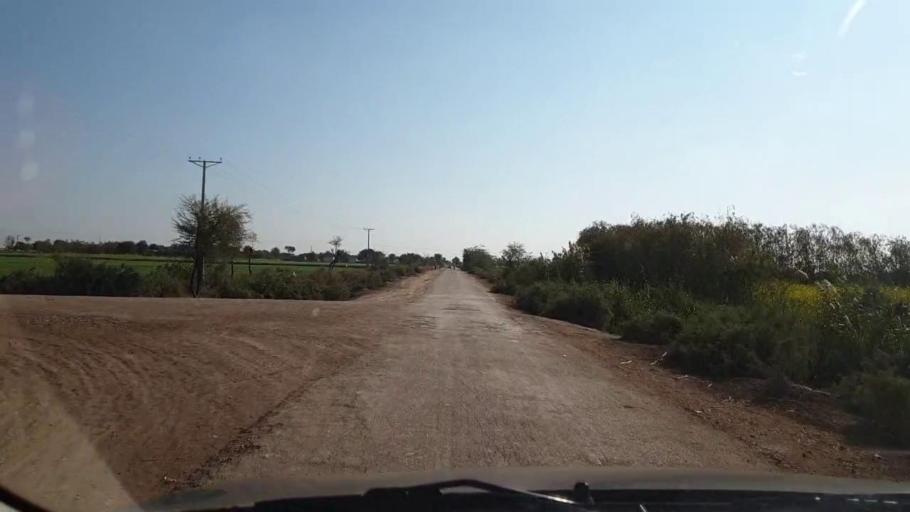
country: PK
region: Sindh
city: Sinjhoro
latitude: 25.9901
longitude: 68.8394
